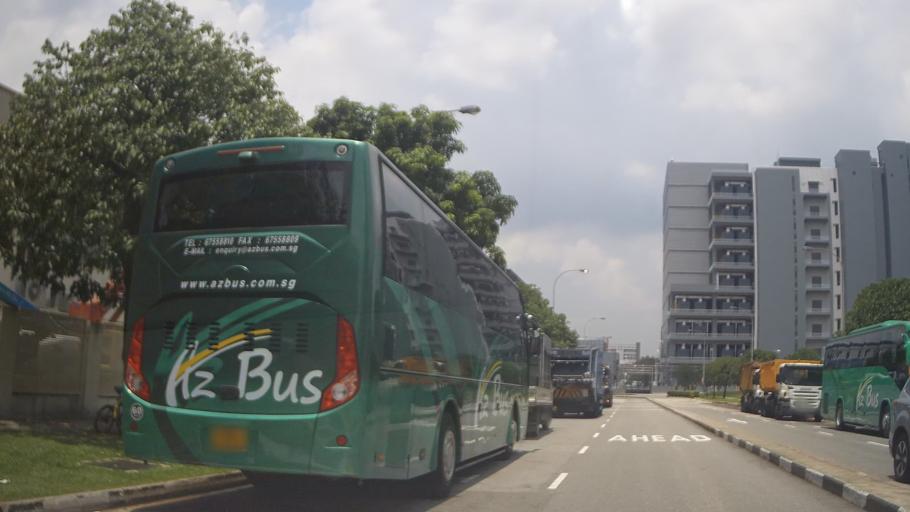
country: MY
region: Johor
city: Johor Bahru
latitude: 1.4503
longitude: 103.7994
